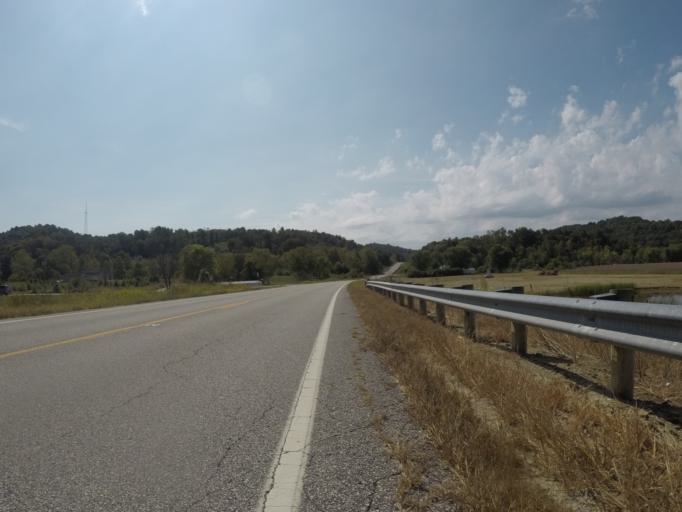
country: US
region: West Virginia
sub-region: Cabell County
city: Lesage
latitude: 38.5099
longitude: -82.3921
